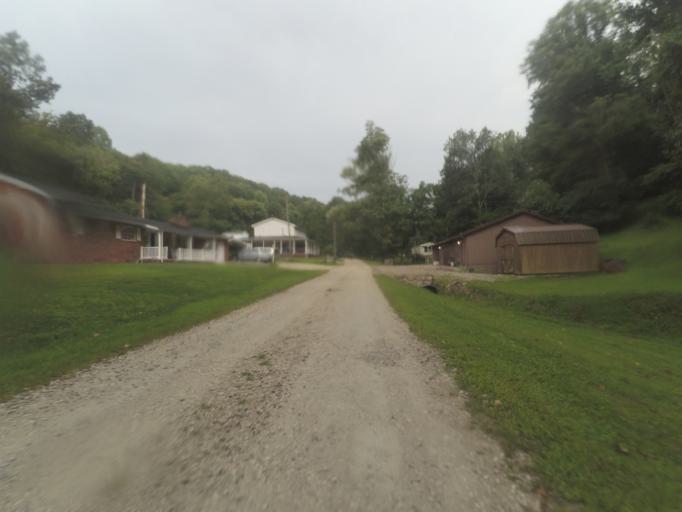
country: US
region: West Virginia
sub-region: Cabell County
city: Huntington
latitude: 38.3799
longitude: -82.3951
